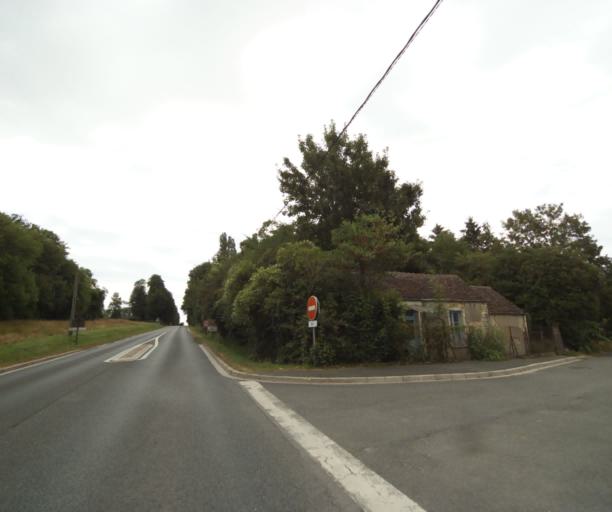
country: FR
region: Ile-de-France
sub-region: Departement de Seine-et-Marne
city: Cely
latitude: 48.4615
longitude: 2.5309
